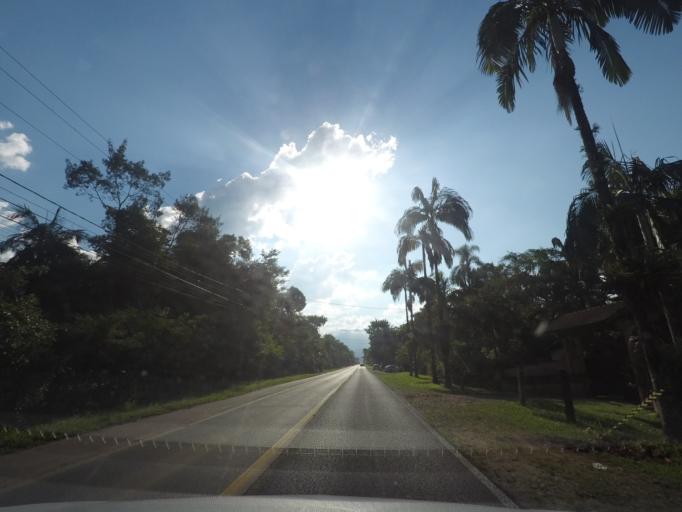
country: BR
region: Parana
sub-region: Antonina
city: Antonina
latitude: -25.4658
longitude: -48.8481
